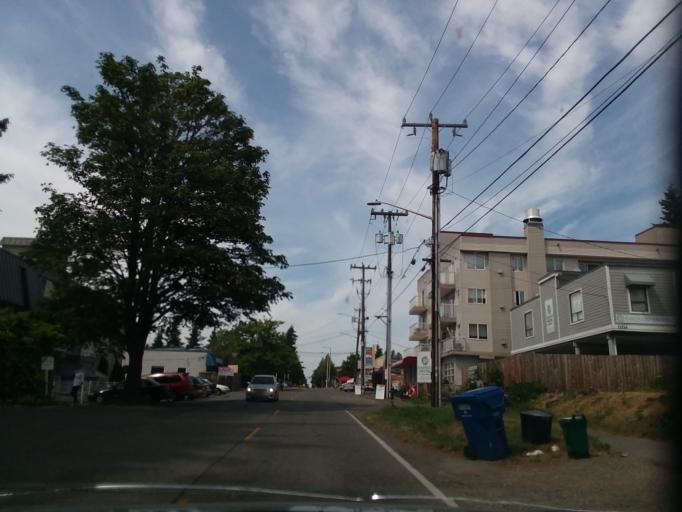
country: US
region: Washington
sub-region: King County
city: Shoreline
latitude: 47.7127
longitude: -122.3125
